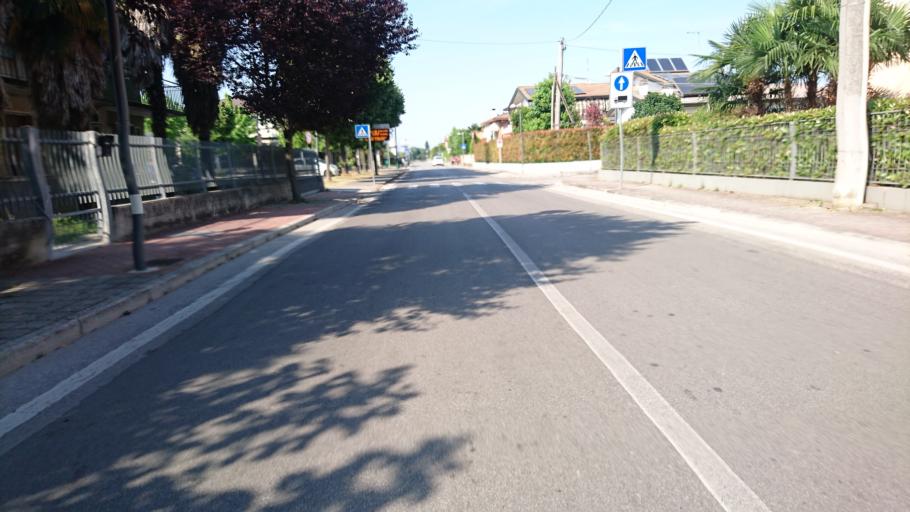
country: IT
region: Veneto
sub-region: Provincia di Padova
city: Terradura
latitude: 45.3478
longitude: 11.8195
